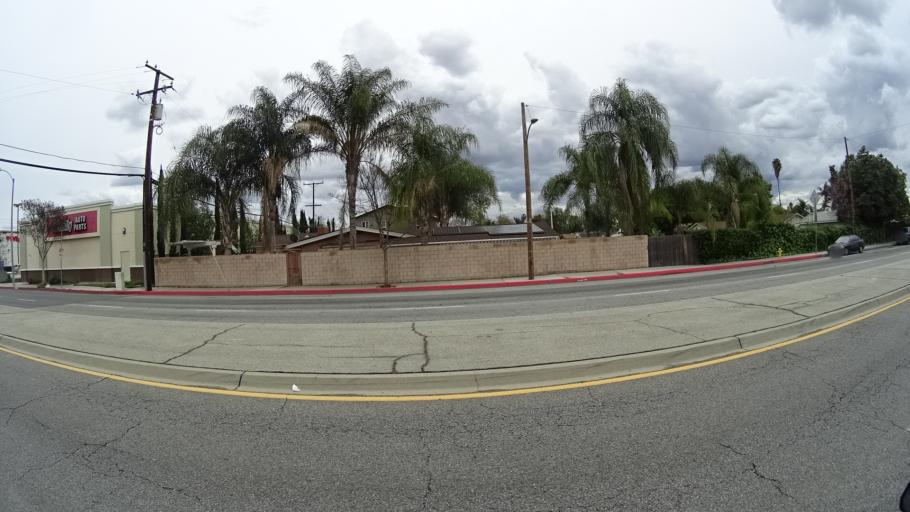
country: US
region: California
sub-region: Los Angeles County
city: West Puente Valley
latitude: 34.0633
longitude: -117.9696
